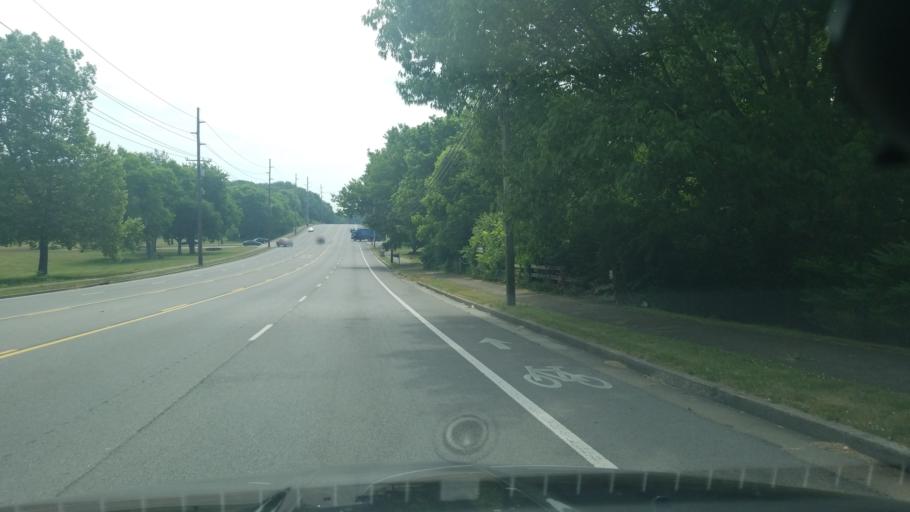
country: US
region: Tennessee
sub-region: Davidson County
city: Goodlettsville
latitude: 36.2677
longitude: -86.7483
